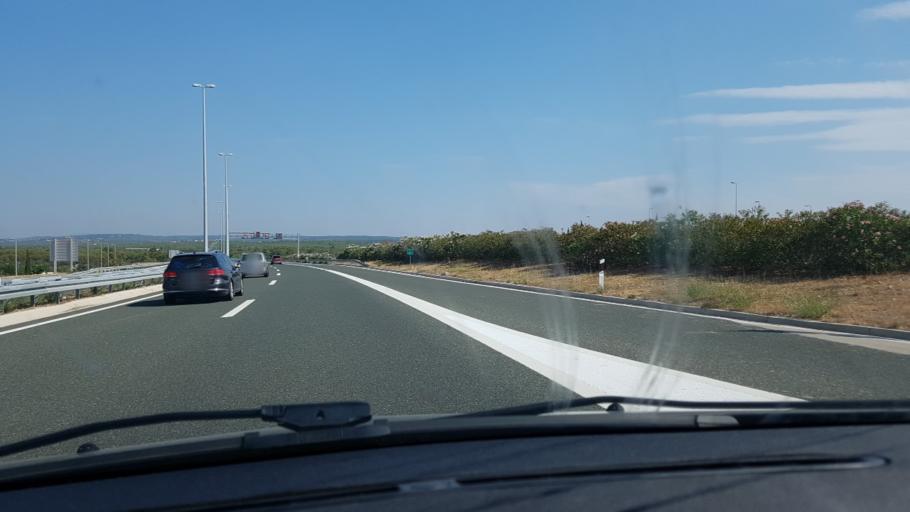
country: HR
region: Sibensko-Kniniska
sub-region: Grad Sibenik
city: Sibenik
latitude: 43.8047
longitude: 15.9176
